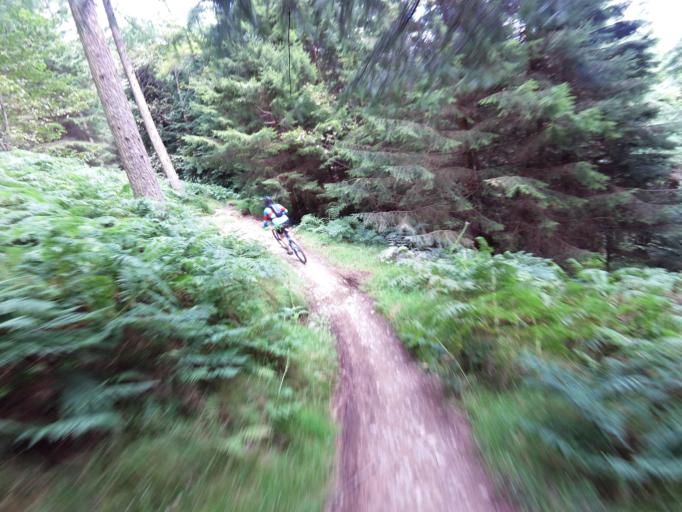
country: GB
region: Scotland
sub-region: The Scottish Borders
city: Peebles
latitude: 55.6628
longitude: -3.1304
